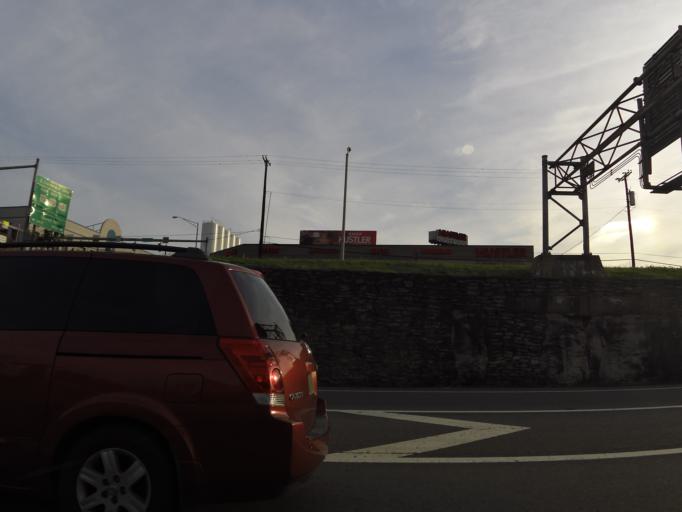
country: US
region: Tennessee
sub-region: Davidson County
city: Nashville
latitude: 36.1585
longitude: -86.7916
